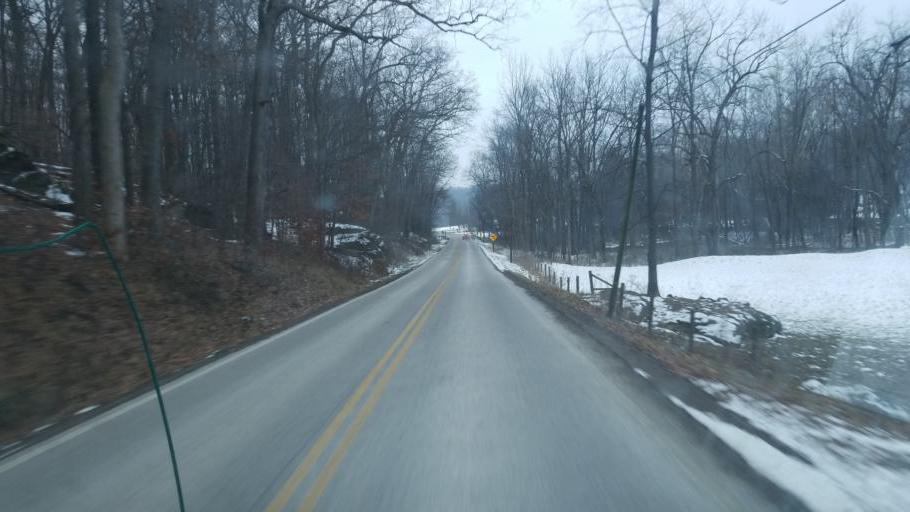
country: US
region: Ohio
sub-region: Sandusky County
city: Bellville
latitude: 40.6556
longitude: -82.3956
